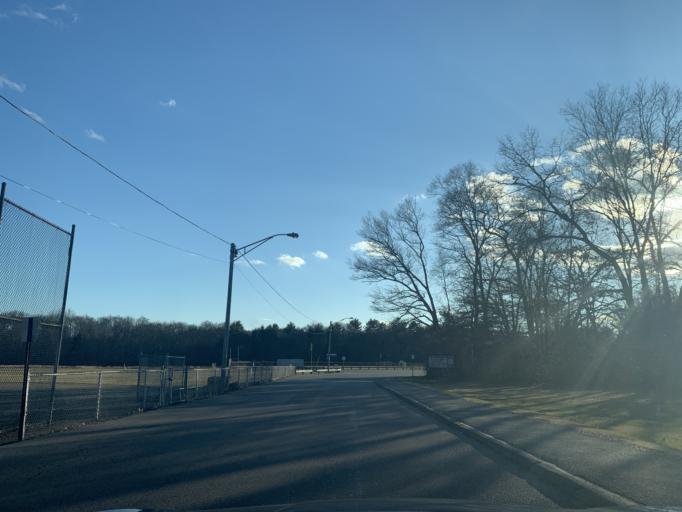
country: US
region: Massachusetts
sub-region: Bristol County
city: Norton
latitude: 41.9619
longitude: -71.1937
